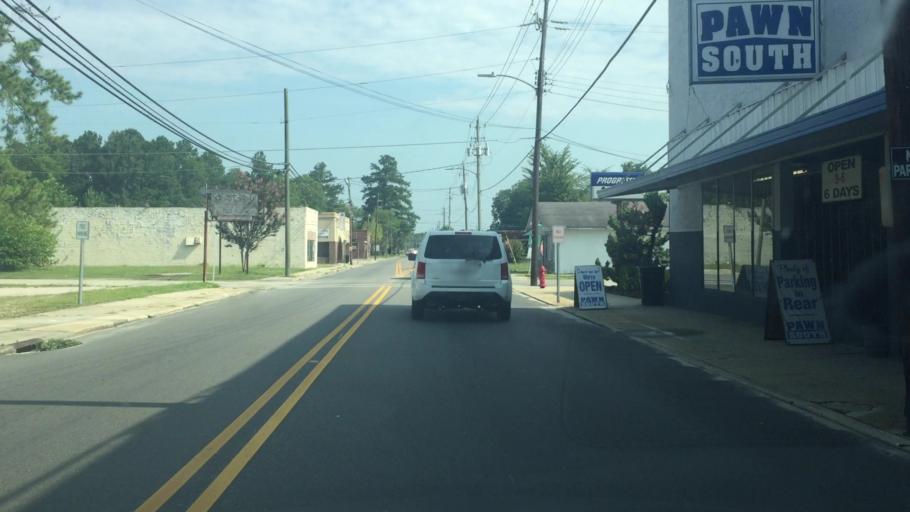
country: US
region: North Carolina
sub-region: Columbus County
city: Chadbourn
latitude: 34.3242
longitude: -78.8264
